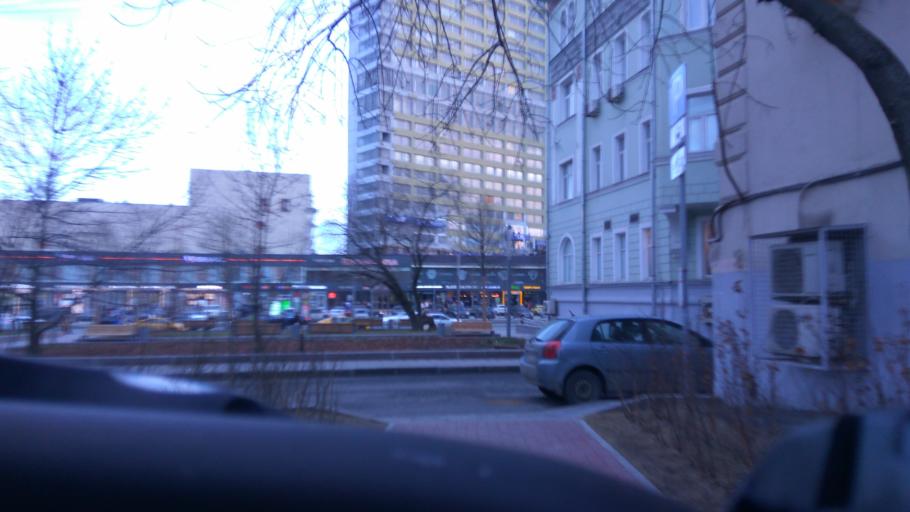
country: RU
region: Moscow
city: Moscow
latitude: 55.7533
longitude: 37.5934
